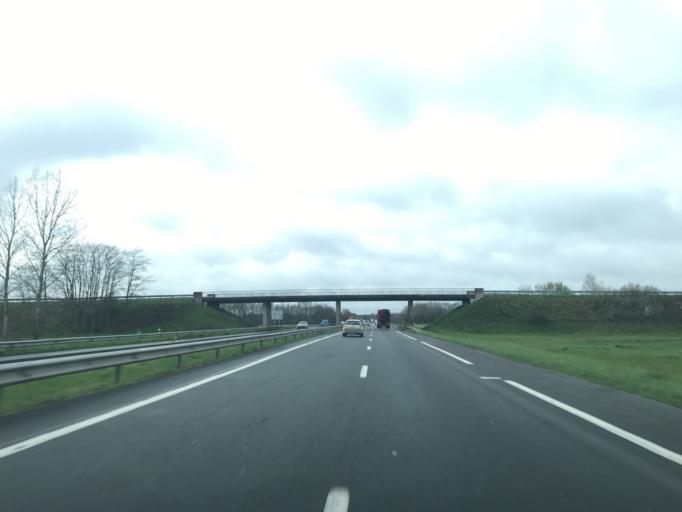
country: FR
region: Centre
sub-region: Departement du Loiret
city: Chateauneuf-sur-Loire
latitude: 47.8879
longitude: 2.2202
